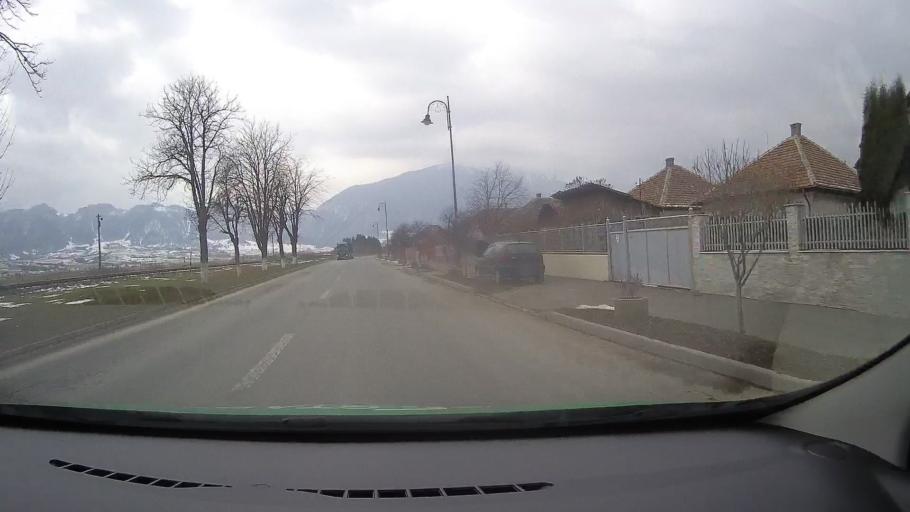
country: RO
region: Brasov
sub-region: Comuna Zarnesti
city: Zarnesti
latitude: 45.5674
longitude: 25.3453
